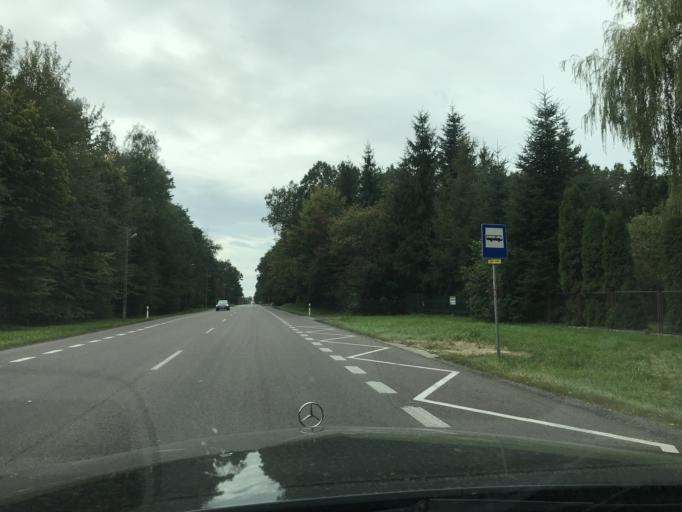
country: PL
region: Lublin Voivodeship
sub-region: Powiat krasnicki
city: Krasnik
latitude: 50.9428
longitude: 22.2709
